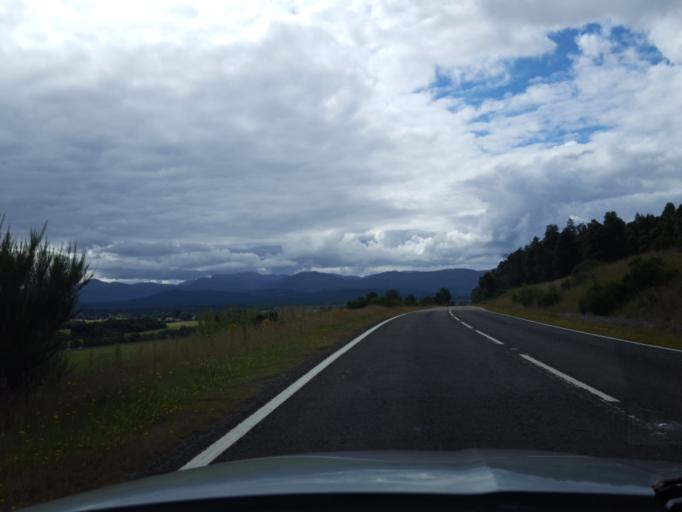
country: GB
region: Scotland
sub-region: Highland
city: Grantown on Spey
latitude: 57.2888
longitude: -3.6668
